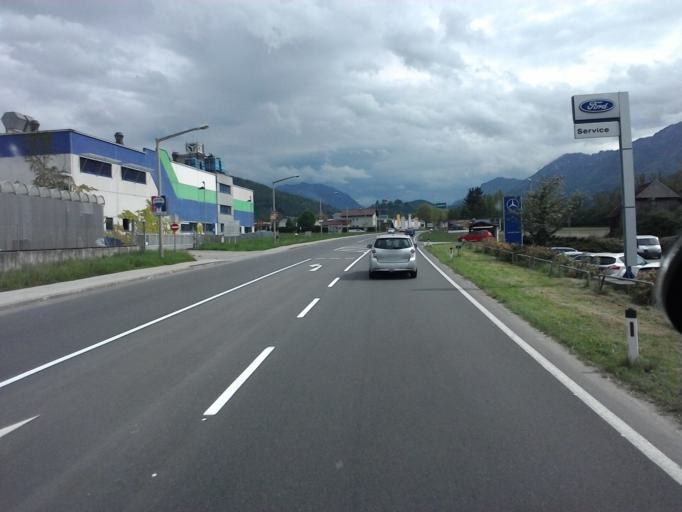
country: AT
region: Upper Austria
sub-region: Politischer Bezirk Kirchdorf an der Krems
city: Micheldorf in Oberoesterreich
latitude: 47.8965
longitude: 14.1276
